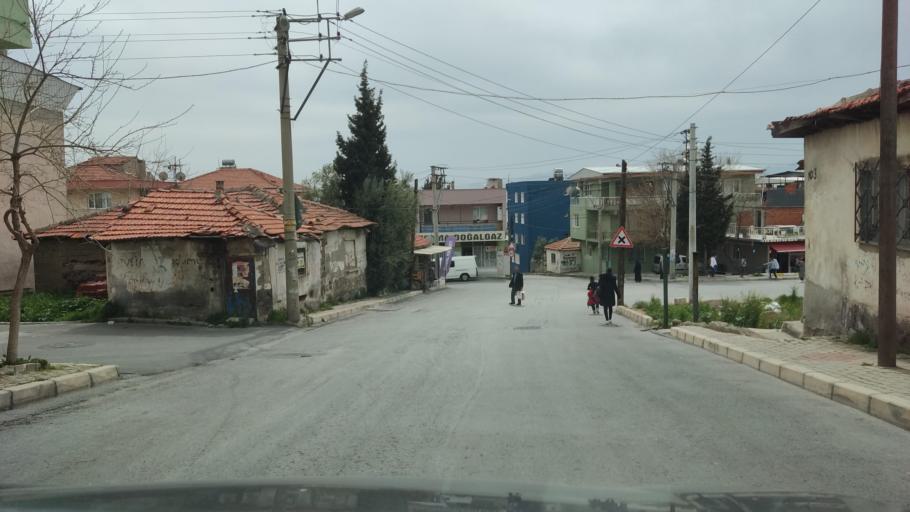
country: TR
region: Izmir
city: Karsiyaka
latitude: 38.4969
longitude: 27.0718
